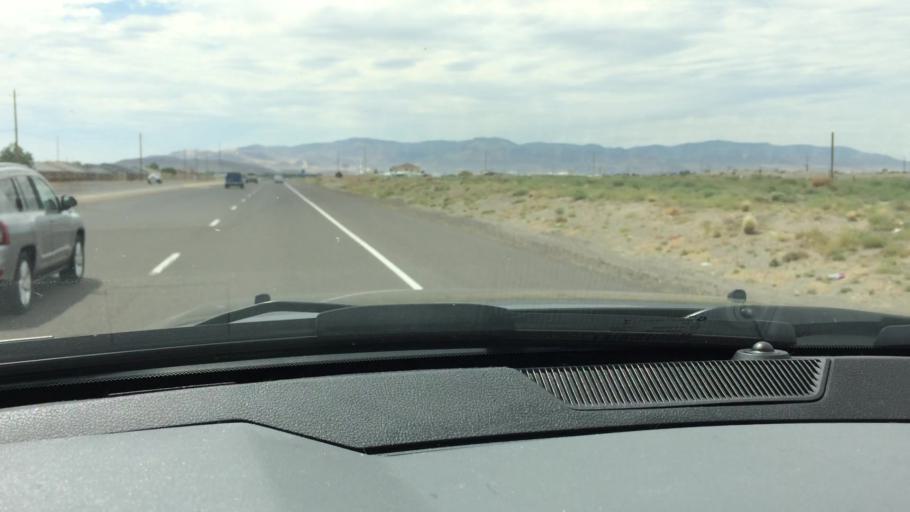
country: US
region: Nevada
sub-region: Lyon County
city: Fernley
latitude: 39.5991
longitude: -119.2020
